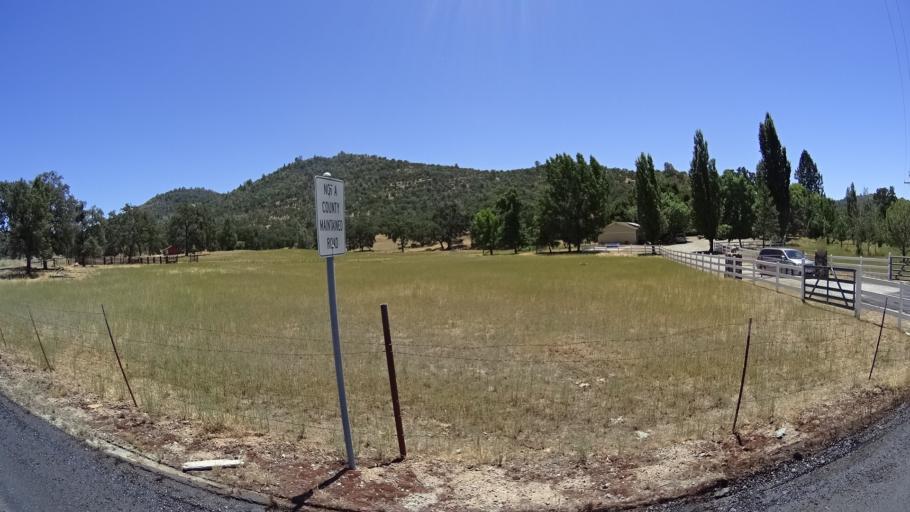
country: US
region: California
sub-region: Calaveras County
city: Copperopolis
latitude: 38.0535
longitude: -120.6210
